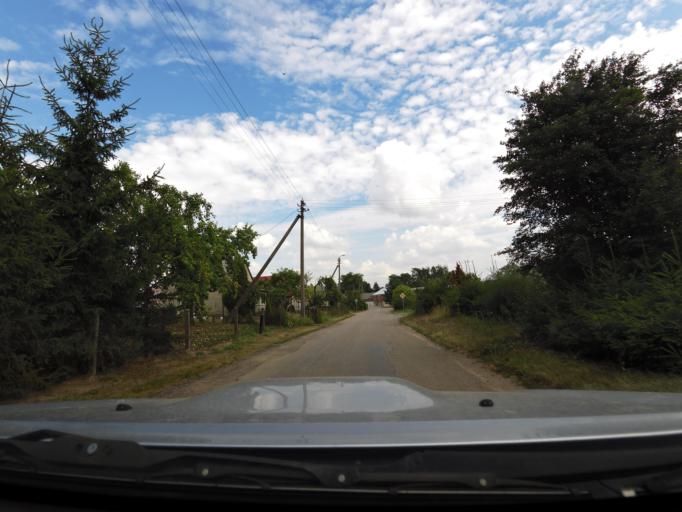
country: LT
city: Gelgaudiskis
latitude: 55.1000
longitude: 22.9795
